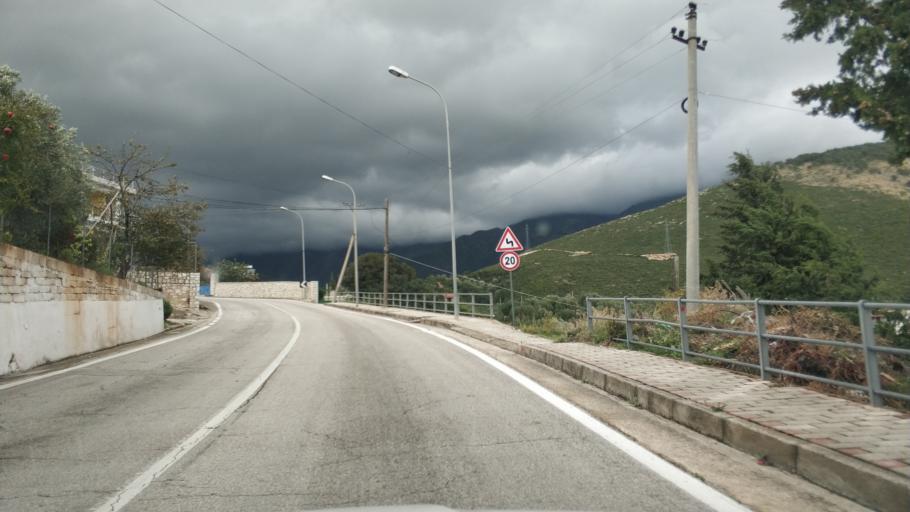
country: AL
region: Vlore
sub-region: Rrethi i Vlores
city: Himare
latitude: 40.1166
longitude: 19.7365
